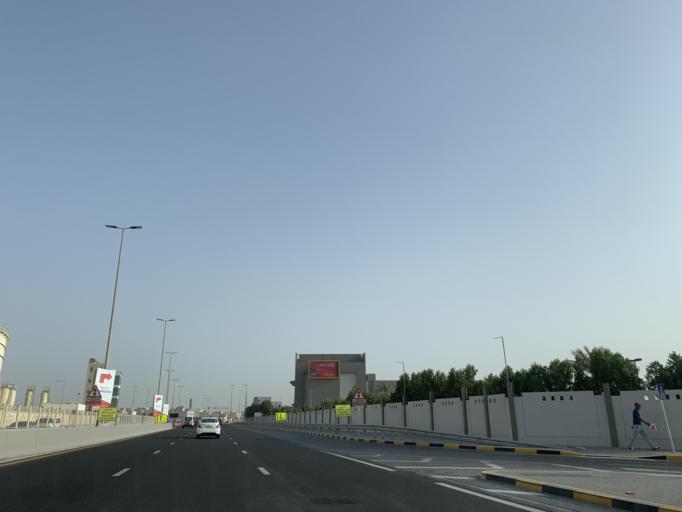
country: BH
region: Northern
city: Madinat `Isa
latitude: 26.1863
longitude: 50.5191
